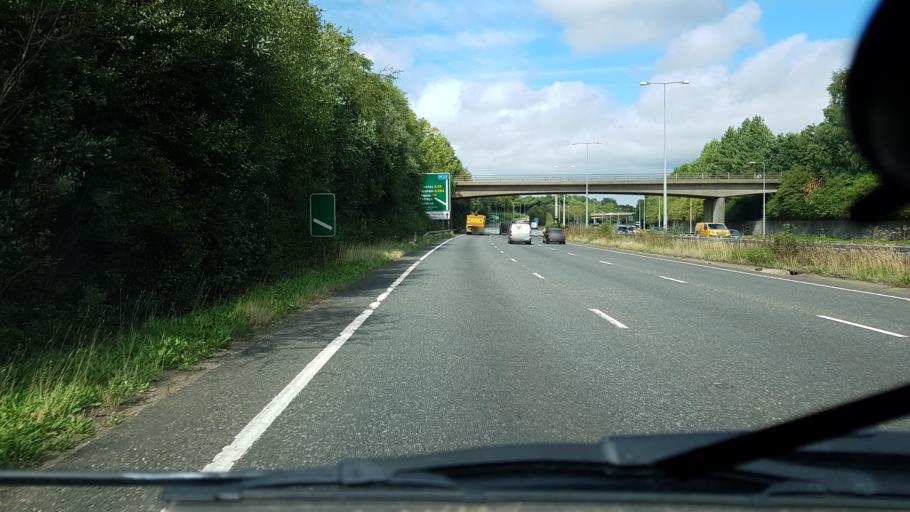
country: GB
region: England
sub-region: West Sussex
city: Broadfield
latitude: 51.0824
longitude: -0.2020
